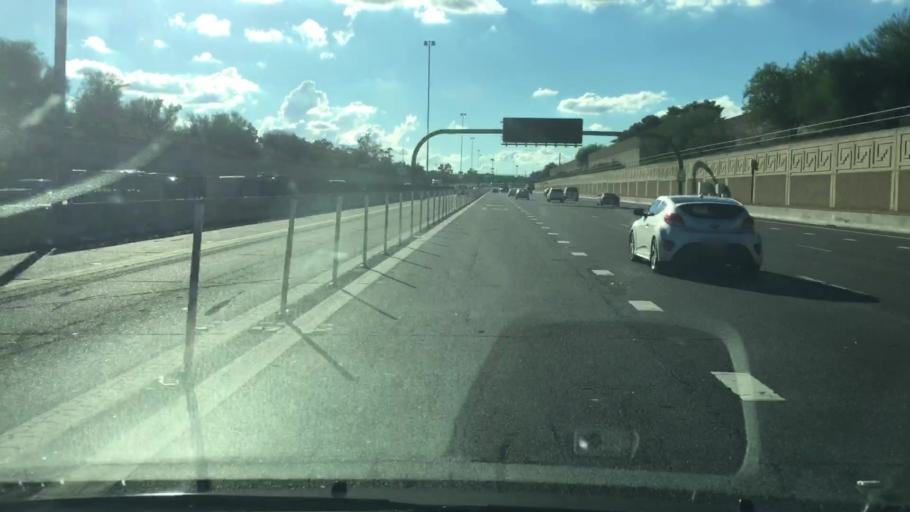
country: US
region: Arizona
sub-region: Maricopa County
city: Guadalupe
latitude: 33.3842
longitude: -111.9462
